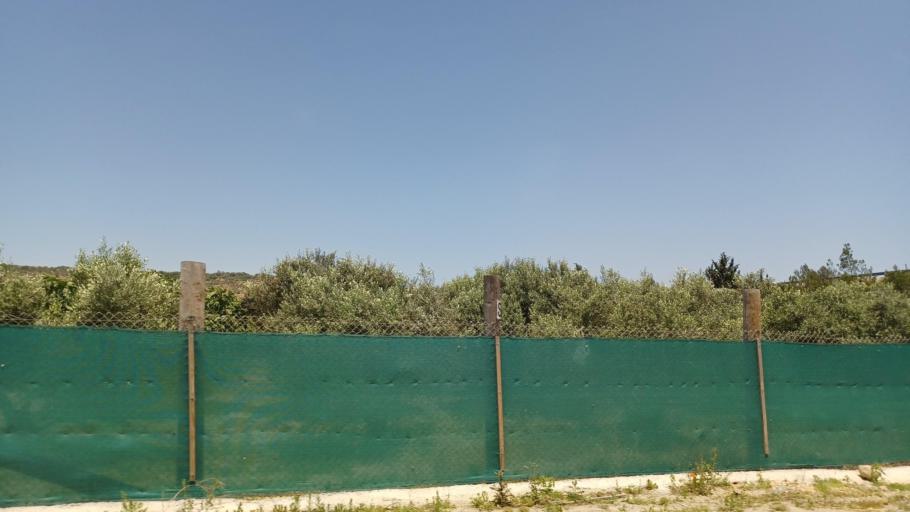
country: CY
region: Larnaka
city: Pyla
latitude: 35.0053
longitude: 33.7014
